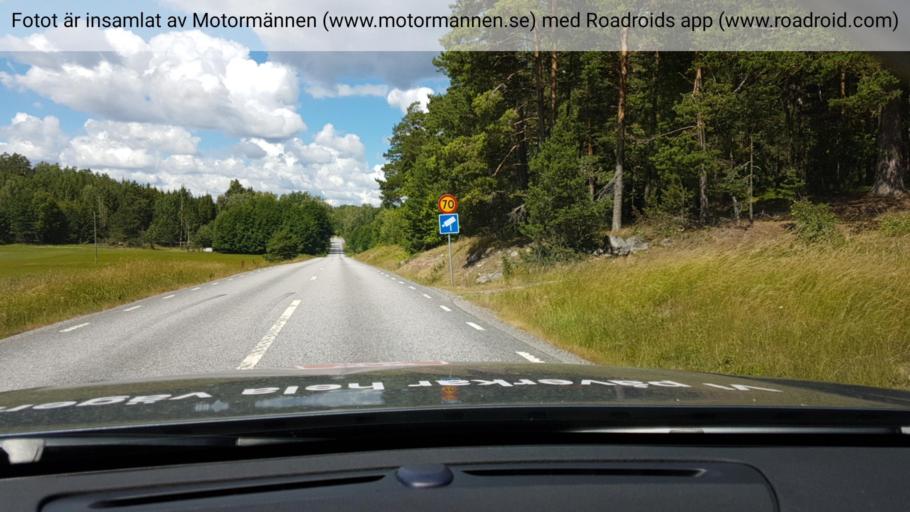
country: SE
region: Stockholm
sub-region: Varmdo Kommun
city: Hemmesta
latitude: 59.3862
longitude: 18.5156
